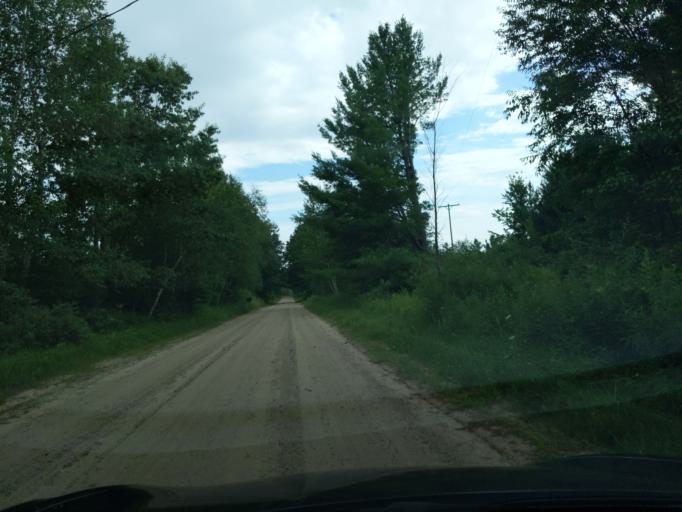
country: US
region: Michigan
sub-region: Clare County
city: Harrison
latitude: 43.9909
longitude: -85.0083
